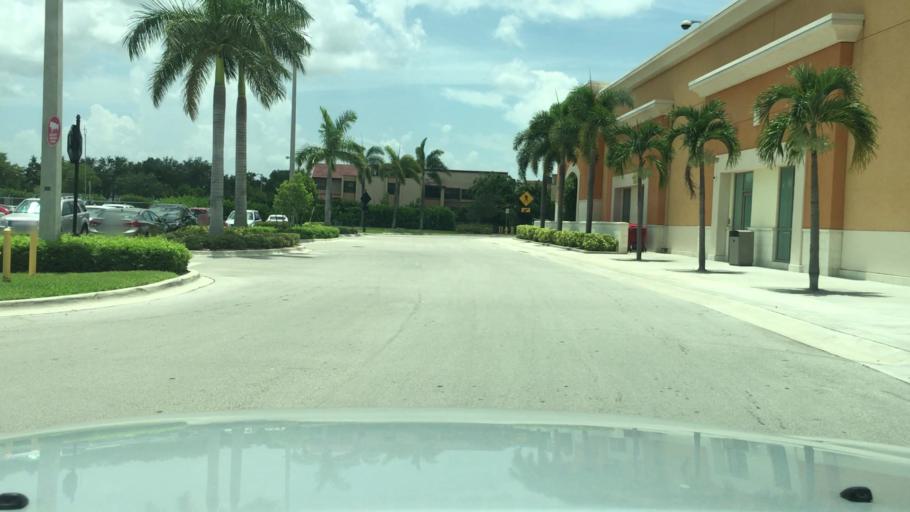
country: US
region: Florida
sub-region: Miami-Dade County
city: Fountainebleau
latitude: 25.7711
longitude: -80.3602
